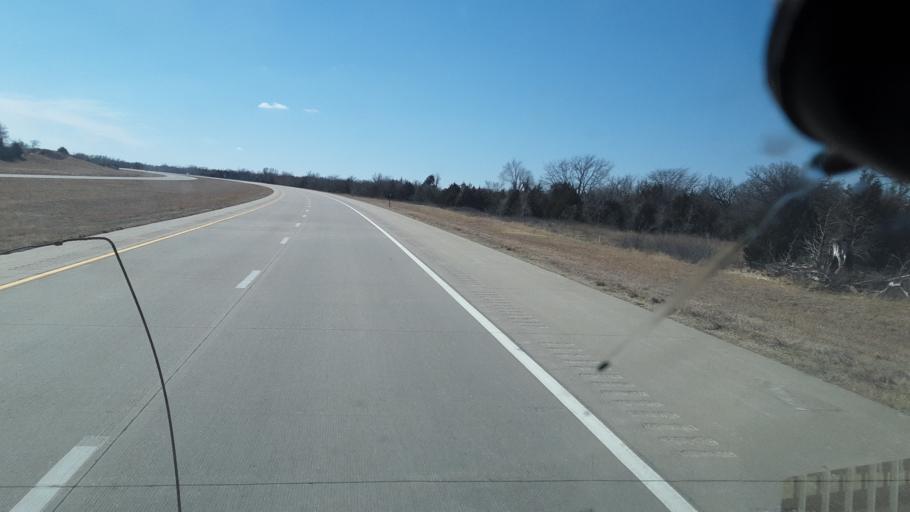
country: US
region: Kansas
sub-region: Reno County
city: Hutchinson
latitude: 38.1439
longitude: -97.8713
